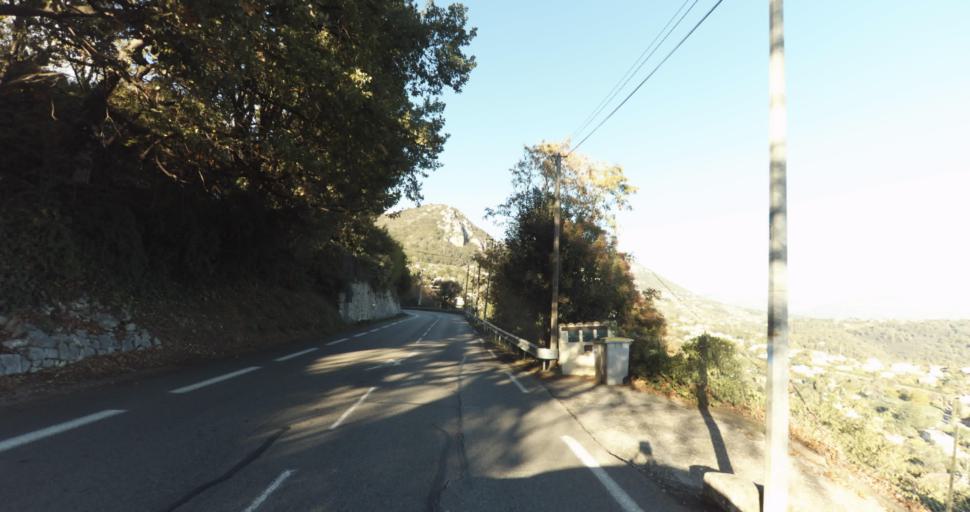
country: FR
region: Provence-Alpes-Cote d'Azur
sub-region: Departement des Alpes-Maritimes
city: Vence
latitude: 43.7294
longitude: 7.1183
